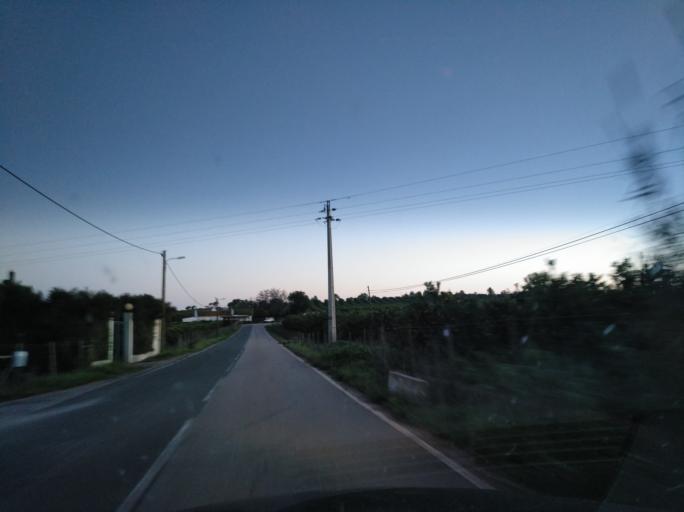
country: PT
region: Faro
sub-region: Vila Real de Santo Antonio
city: Monte Gordo
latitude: 37.1980
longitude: -7.5128
